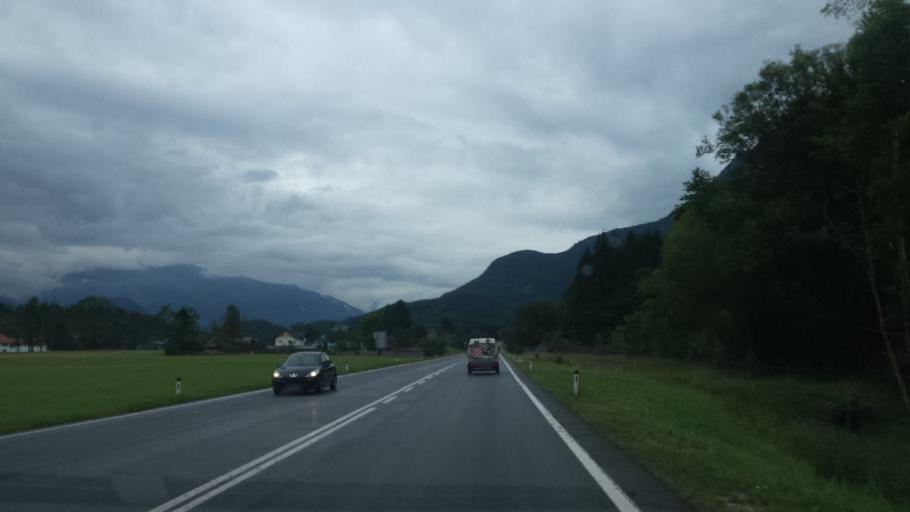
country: AT
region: Salzburg
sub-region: Politischer Bezirk Salzburg-Umgebung
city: Strobl
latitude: 47.7137
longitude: 13.5294
